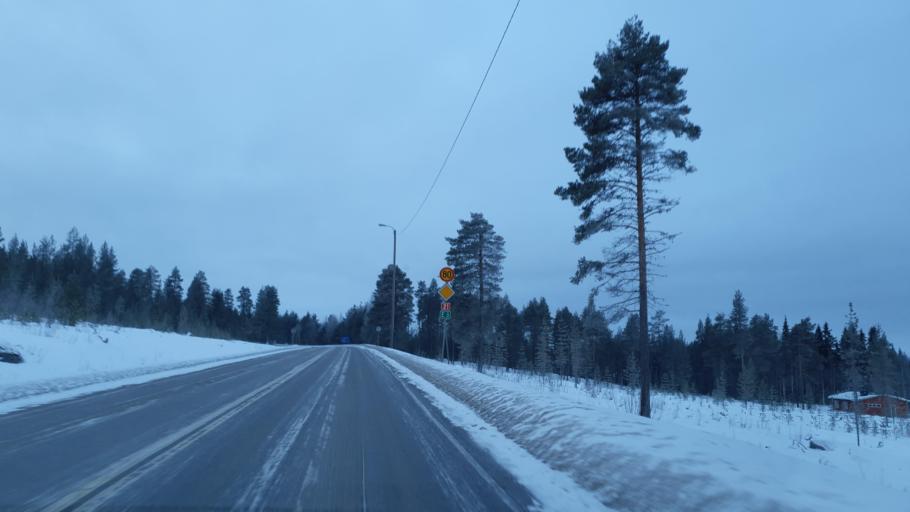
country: SE
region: Norrbotten
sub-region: Overtornea Kommun
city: OEvertornea
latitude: 66.5389
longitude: 23.8397
